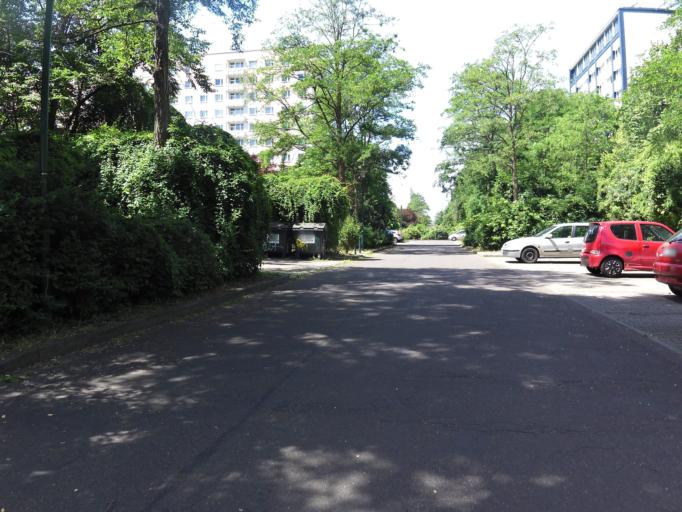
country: DE
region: Saxony
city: Markkleeberg
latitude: 51.3012
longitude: 12.4007
